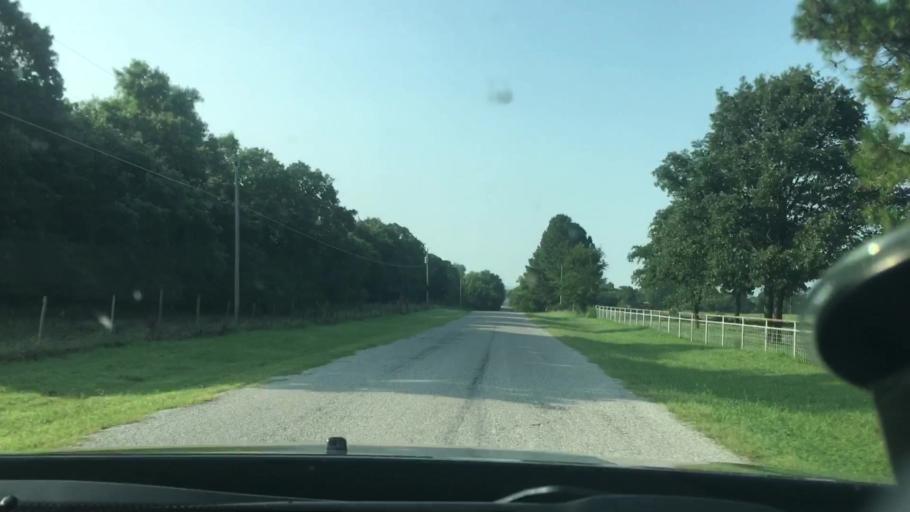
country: US
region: Oklahoma
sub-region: Pontotoc County
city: Ada
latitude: 34.7946
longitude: -96.7397
